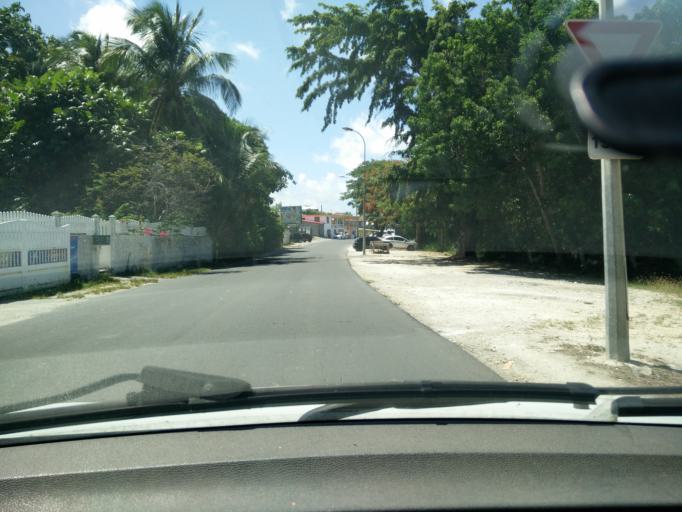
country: GP
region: Guadeloupe
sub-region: Guadeloupe
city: Le Moule
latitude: 16.3276
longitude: -61.3423
